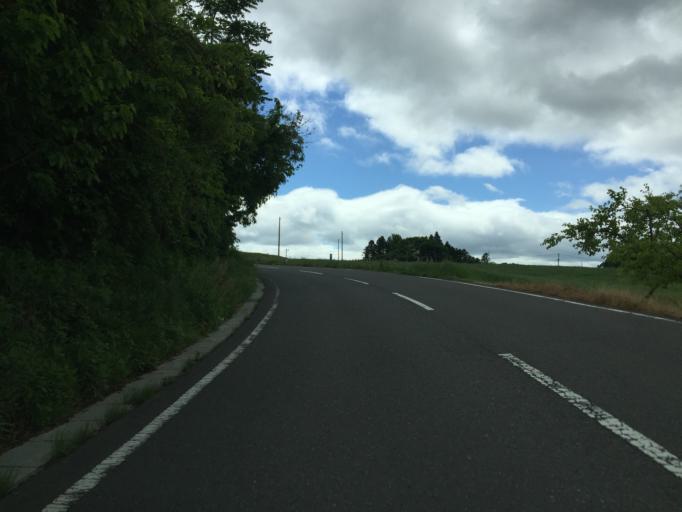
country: JP
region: Fukushima
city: Miharu
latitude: 37.4852
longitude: 140.4636
